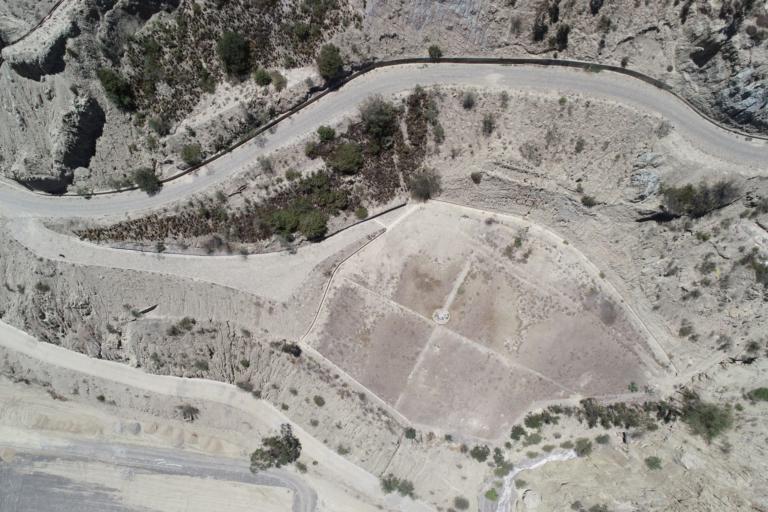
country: BO
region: La Paz
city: La Paz
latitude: -16.6184
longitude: -68.0598
